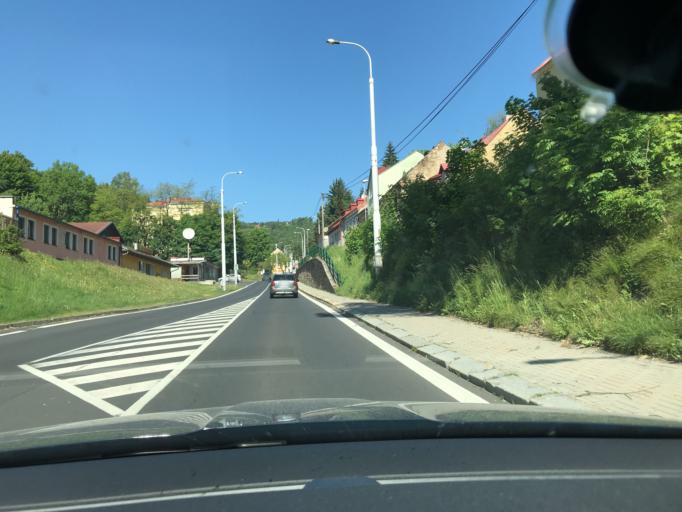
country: CZ
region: Karlovarsky
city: Jachymov
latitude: 50.3630
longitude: 12.9275
